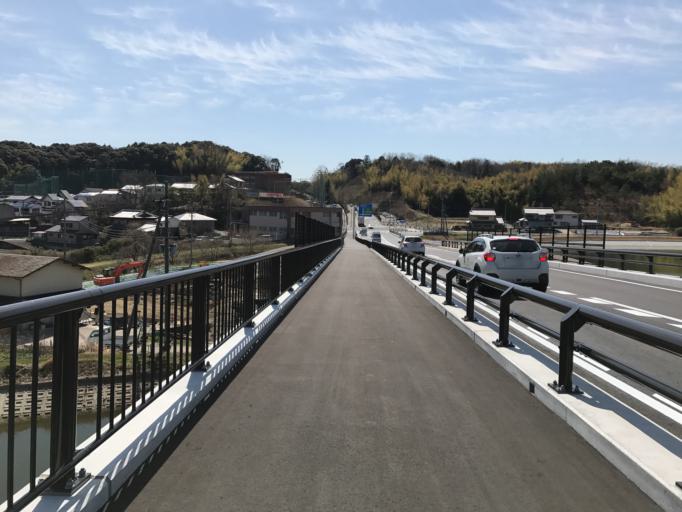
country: JP
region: Kyoto
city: Tanabe
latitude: 34.7787
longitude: 135.7821
